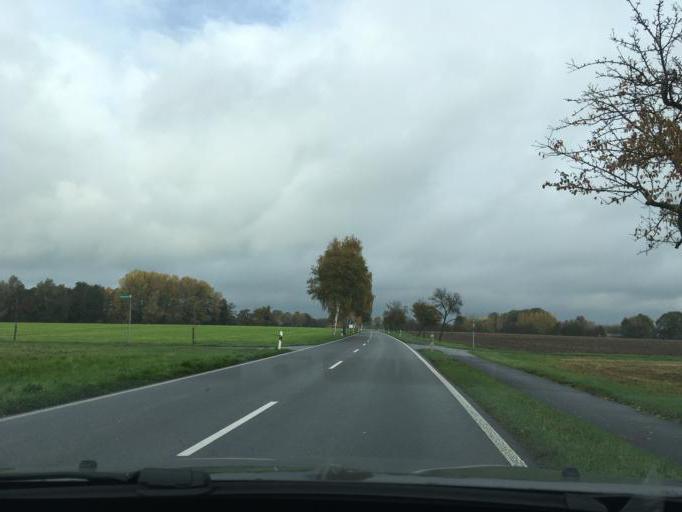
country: DE
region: North Rhine-Westphalia
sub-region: Regierungsbezirk Munster
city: Vreden
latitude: 52.0560
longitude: 6.8015
